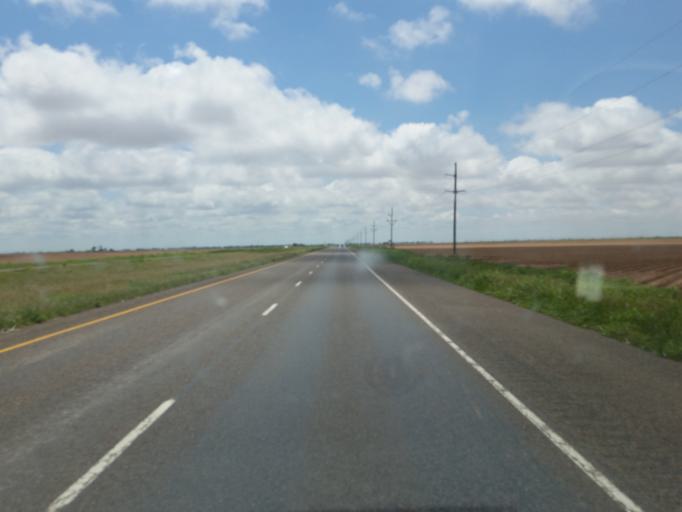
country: US
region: Texas
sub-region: Lubbock County
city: Slaton
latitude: 33.3866
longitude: -101.5940
